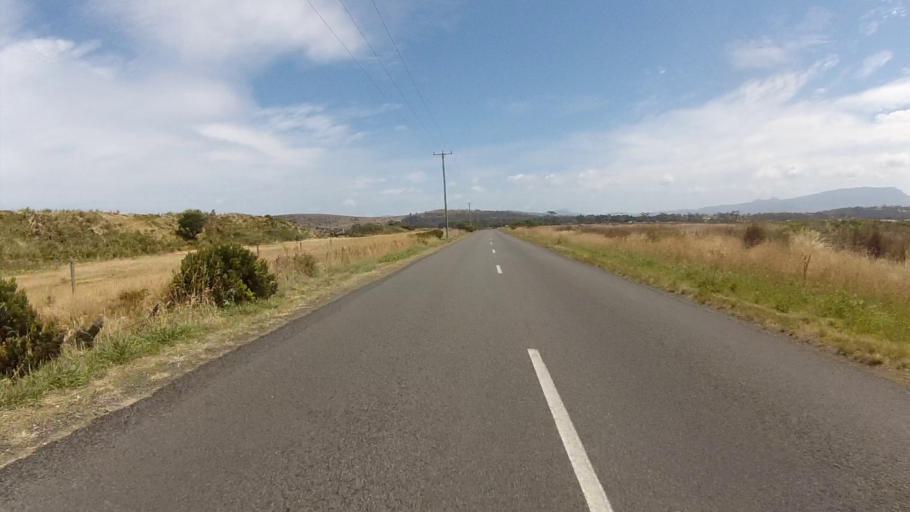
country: AU
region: Tasmania
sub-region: Clarence
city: Sandford
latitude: -43.0329
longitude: 147.4505
